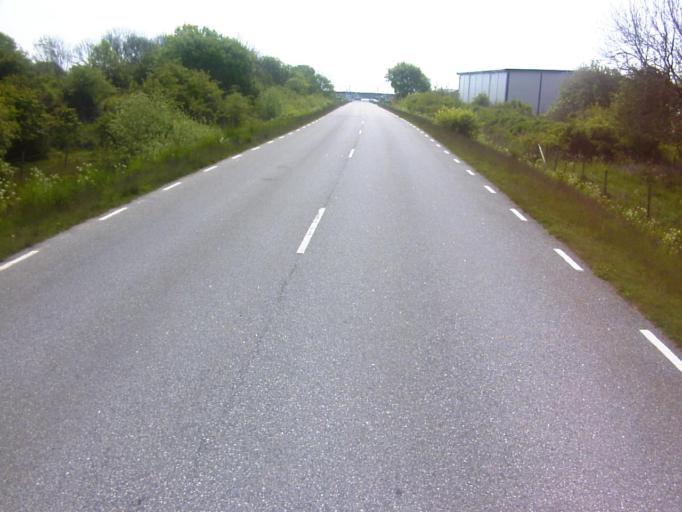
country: SE
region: Blekinge
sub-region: Solvesborgs Kommun
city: Soelvesborg
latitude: 56.0039
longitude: 14.7277
